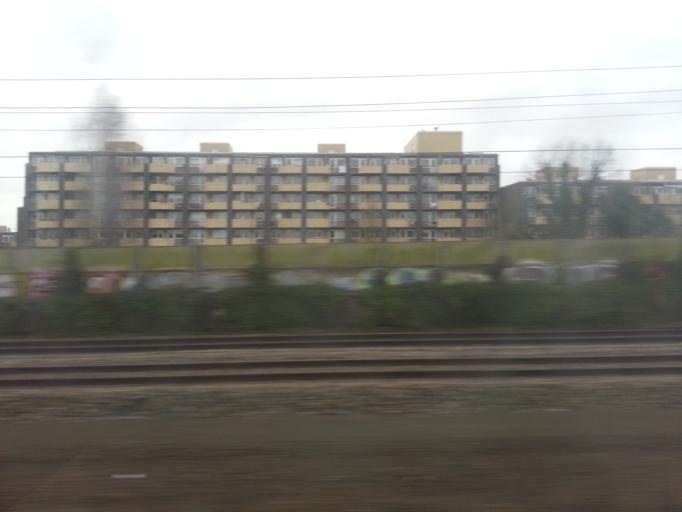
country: NL
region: South Holland
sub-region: Gemeente Zwijndrecht
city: Zwijndrecht
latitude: 51.8143
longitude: 4.6435
